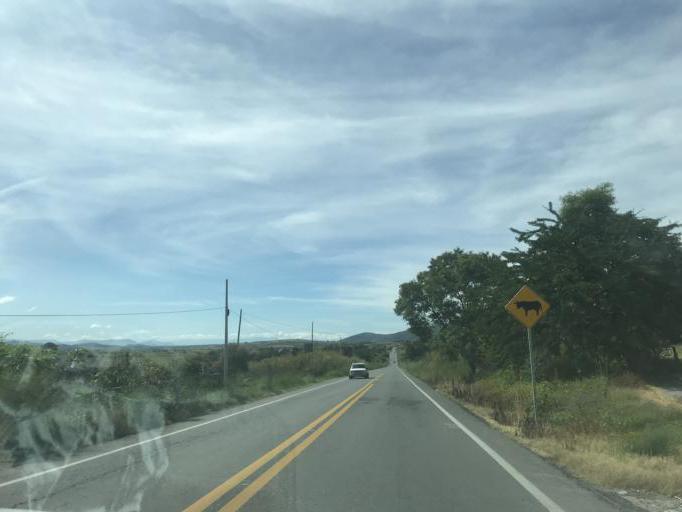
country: MX
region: Guerrero
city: Tepecoacuilco de Trujano
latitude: 18.2772
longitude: -99.5157
